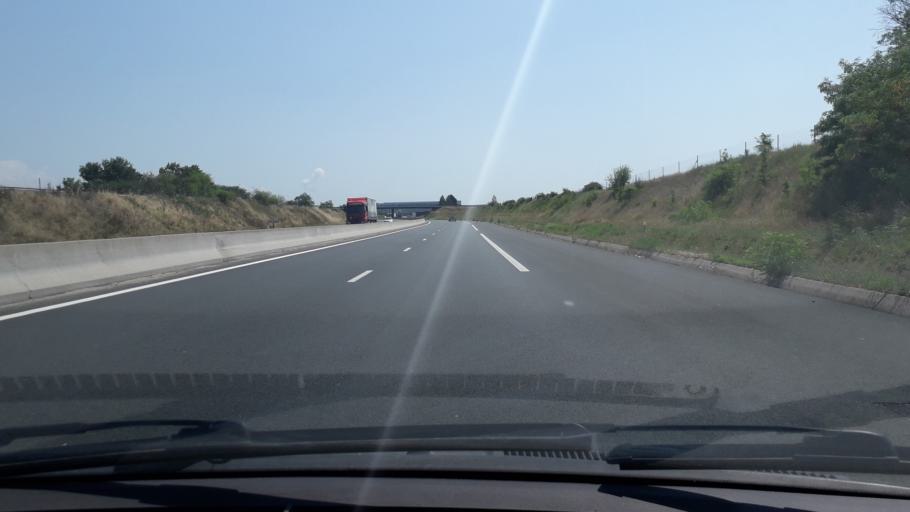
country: FR
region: Rhone-Alpes
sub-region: Departement du Rhone
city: Pusignan
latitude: 45.7662
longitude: 5.0622
